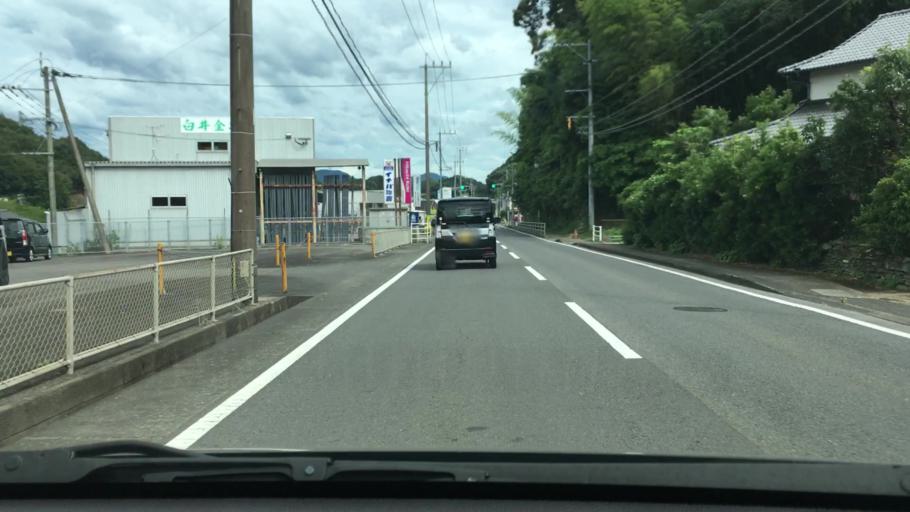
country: JP
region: Nagasaki
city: Togitsu
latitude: 32.8898
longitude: 129.7846
